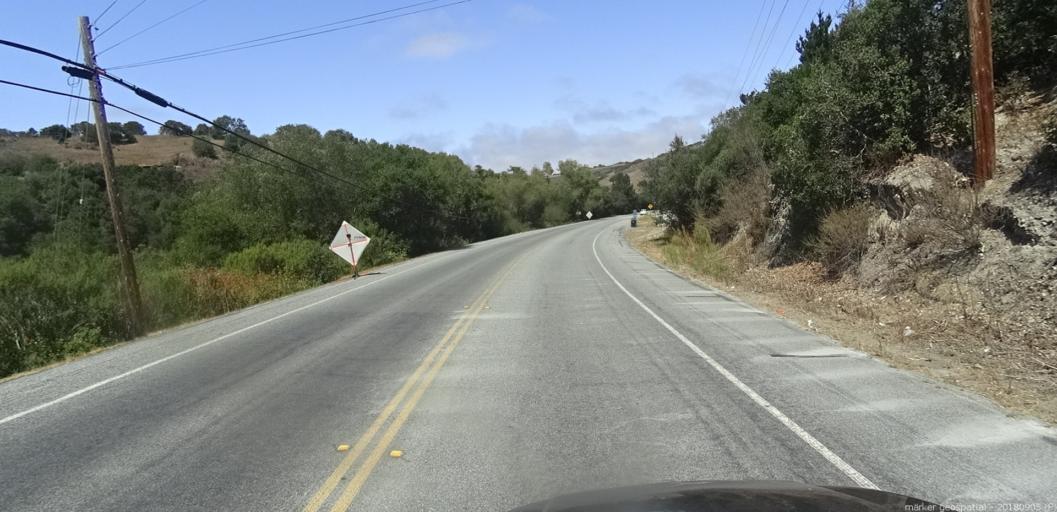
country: US
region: California
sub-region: Monterey County
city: Carmel Valley Village
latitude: 36.5670
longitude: -121.7550
